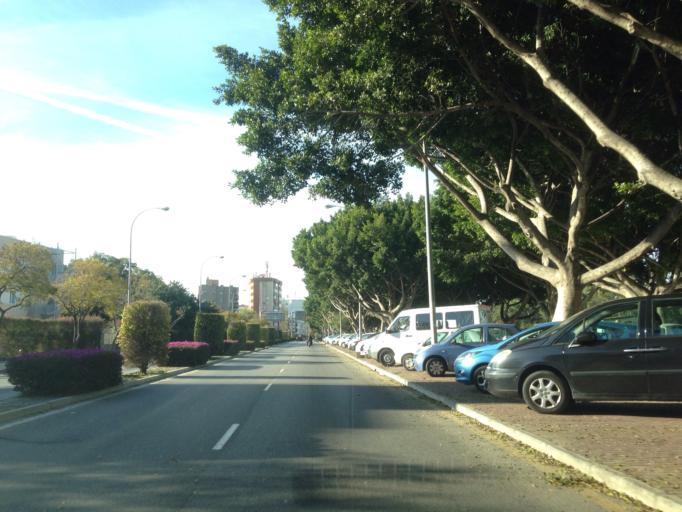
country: ES
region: Andalusia
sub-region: Provincia de Malaga
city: Malaga
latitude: 36.7323
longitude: -4.4252
